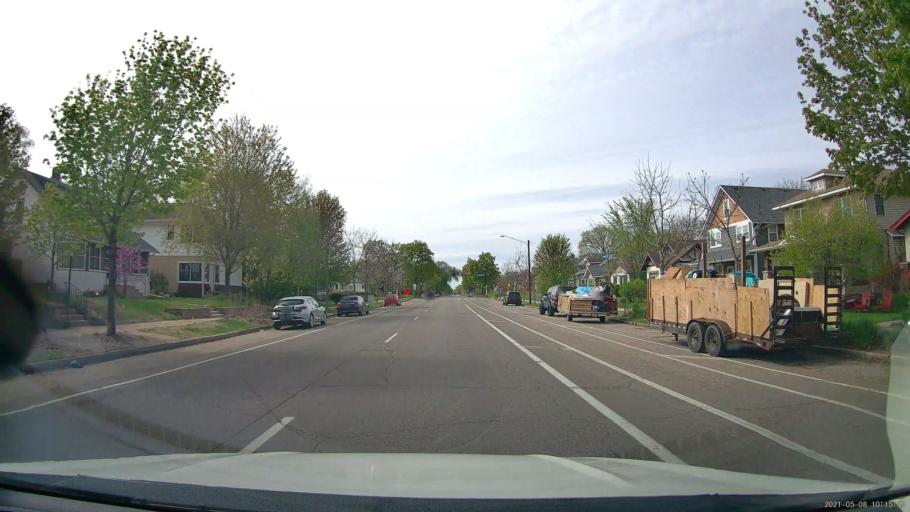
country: US
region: Minnesota
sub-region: Hennepin County
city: Richfield
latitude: 44.9279
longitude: -93.2675
